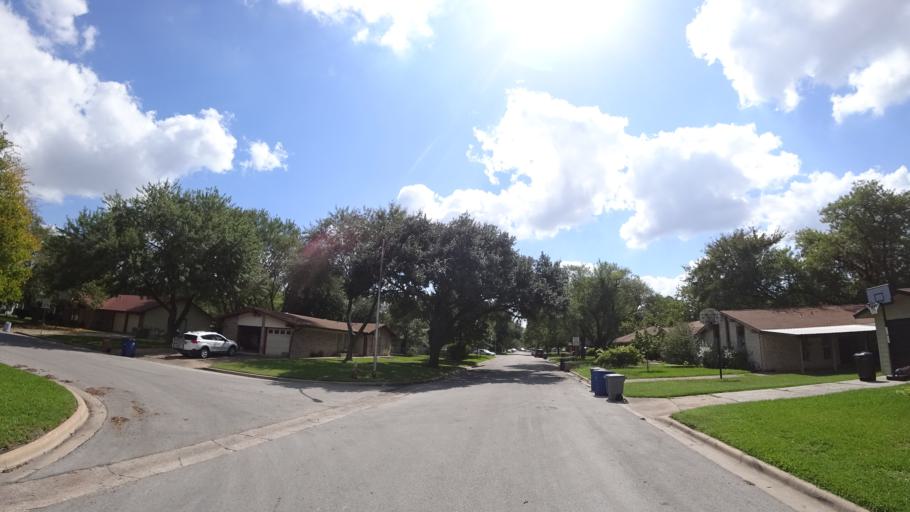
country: US
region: Texas
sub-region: Travis County
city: Wells Branch
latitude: 30.3653
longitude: -97.7231
